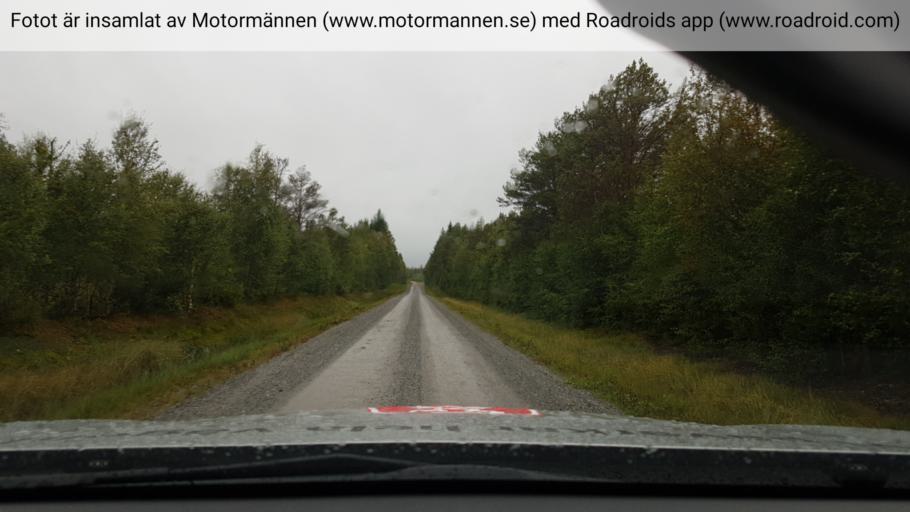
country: SE
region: Vaesterbotten
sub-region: Asele Kommun
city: Asele
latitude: 64.0122
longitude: 17.6241
